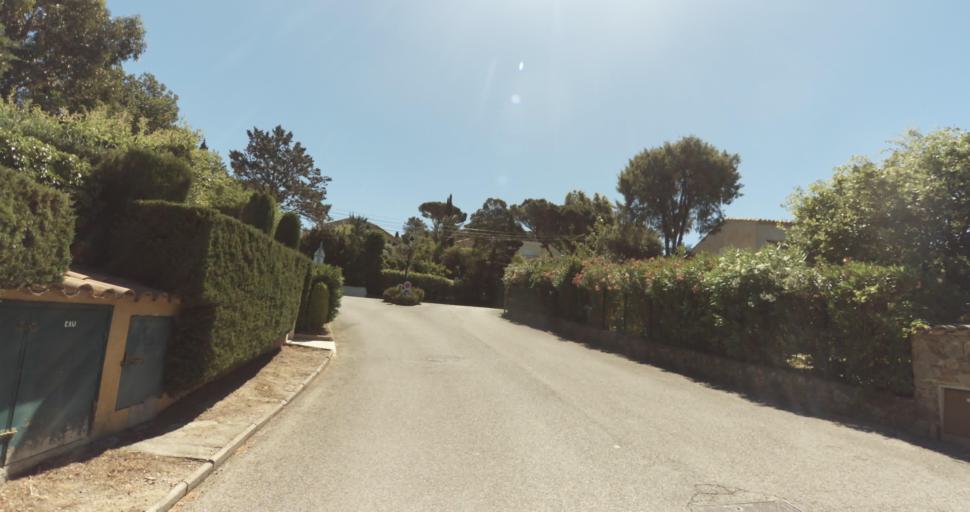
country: FR
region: Provence-Alpes-Cote d'Azur
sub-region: Departement du Var
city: Gassin
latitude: 43.2601
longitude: 6.5995
